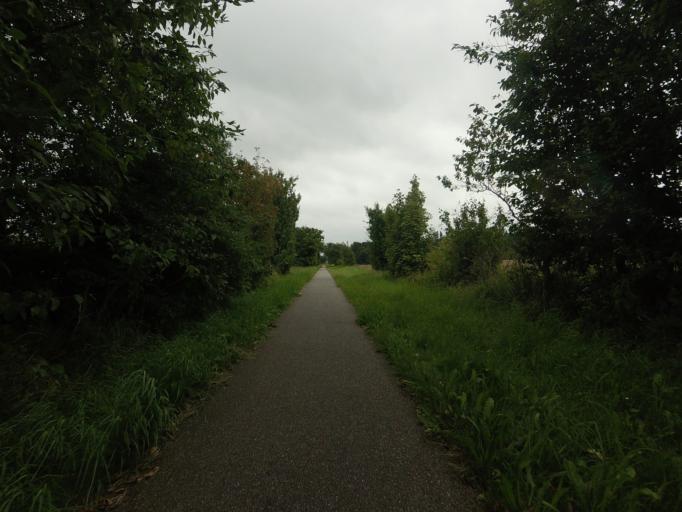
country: DK
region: Central Jutland
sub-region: Horsens Kommune
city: Braedstrup
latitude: 55.9941
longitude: 9.5893
